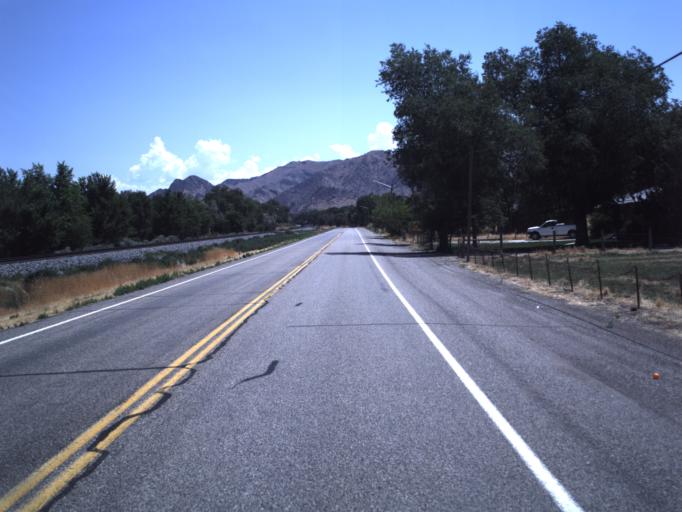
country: US
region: Utah
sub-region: Millard County
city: Delta
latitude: 39.5338
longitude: -112.2969
